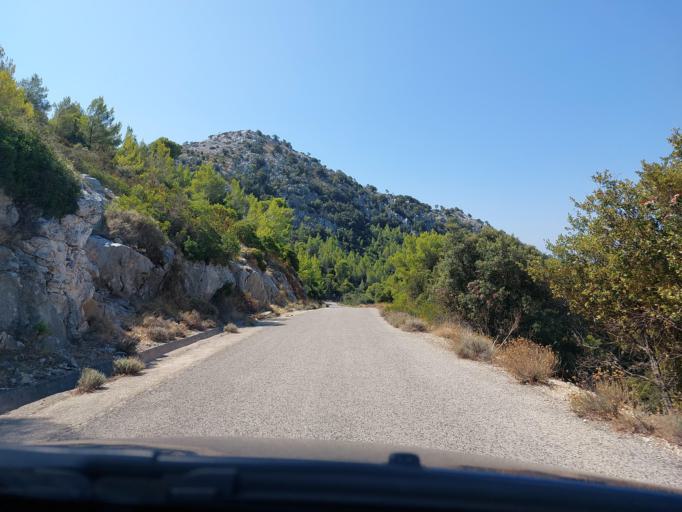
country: HR
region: Dubrovacko-Neretvanska
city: Smokvica
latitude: 42.7456
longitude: 16.8481
